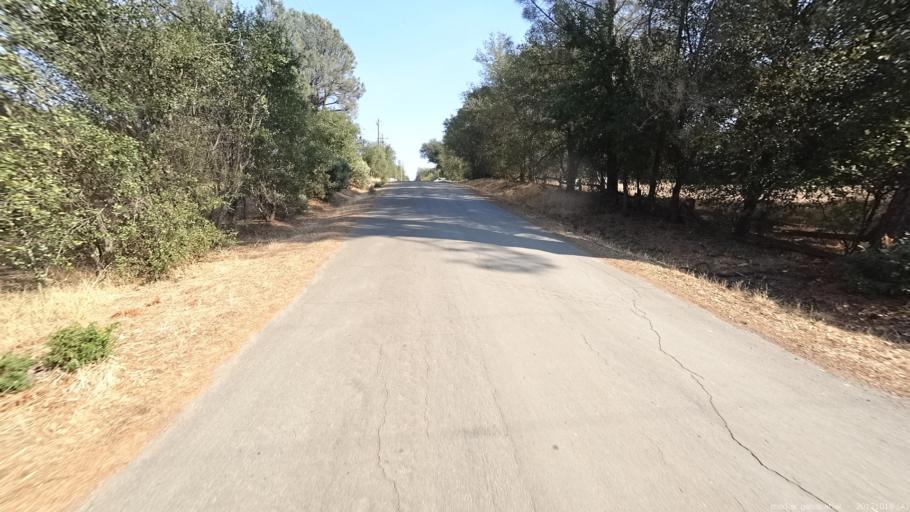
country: US
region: California
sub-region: Shasta County
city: Palo Cedro
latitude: 40.5529
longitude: -122.2837
